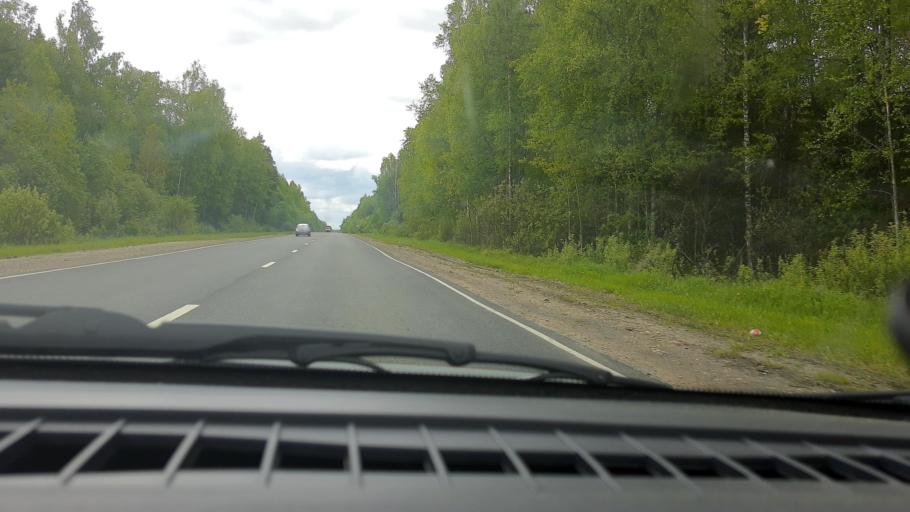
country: RU
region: Nizjnij Novgorod
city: Vladimirskoye
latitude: 56.9427
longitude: 45.0807
